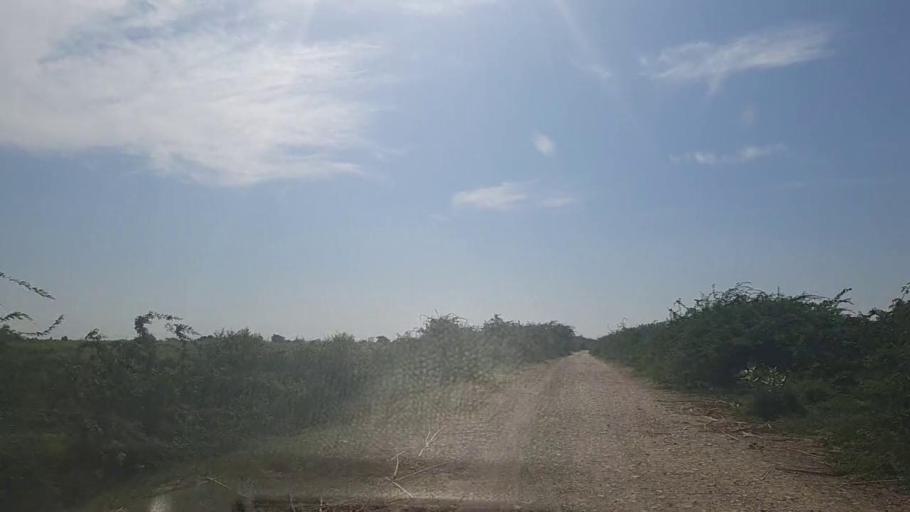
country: PK
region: Sindh
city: Mirpur Batoro
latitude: 24.6785
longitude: 68.1824
